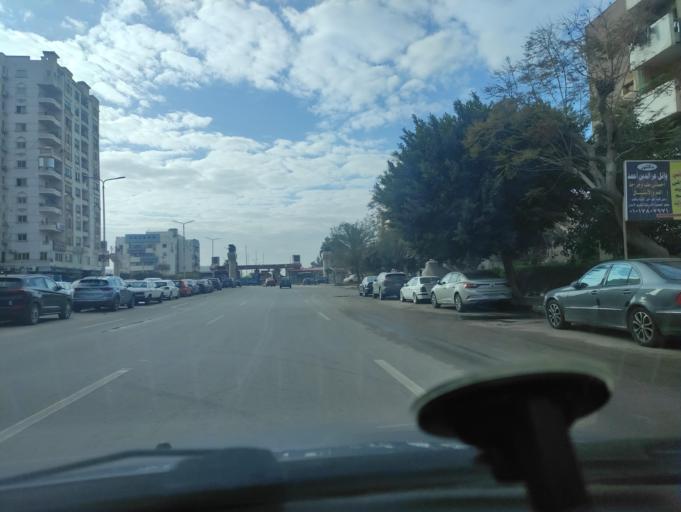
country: EG
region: Muhafazat al Qahirah
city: Cairo
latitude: 30.0473
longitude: 31.3512
